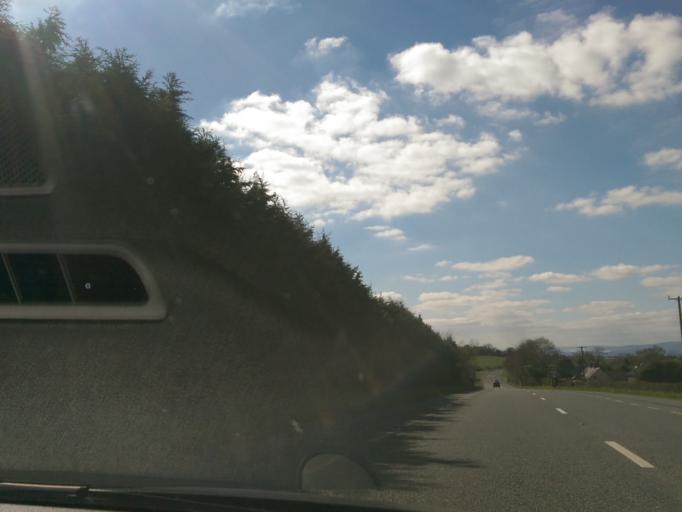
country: IE
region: Leinster
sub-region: Laois
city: Stradbally
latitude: 53.0266
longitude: -7.2139
